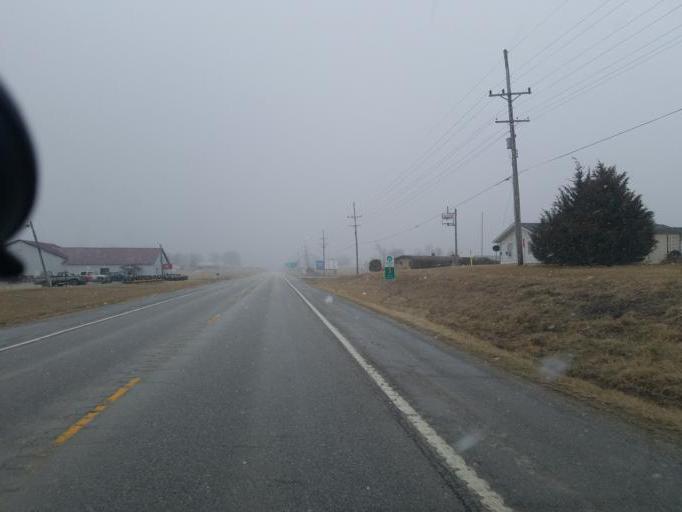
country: US
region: Missouri
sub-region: Adair County
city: Kirksville
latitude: 40.2512
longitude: -92.5826
